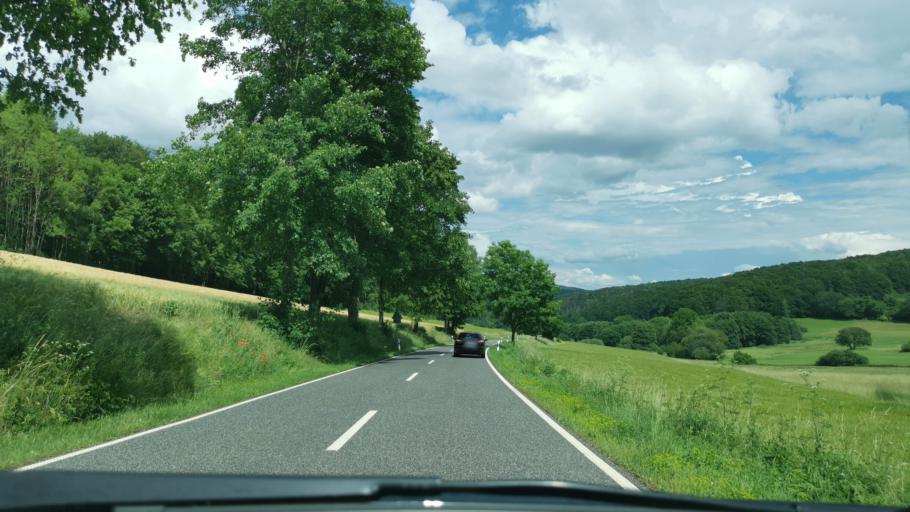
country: DE
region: Hesse
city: Hessisch Lichtenau
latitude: 51.1697
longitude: 9.7832
